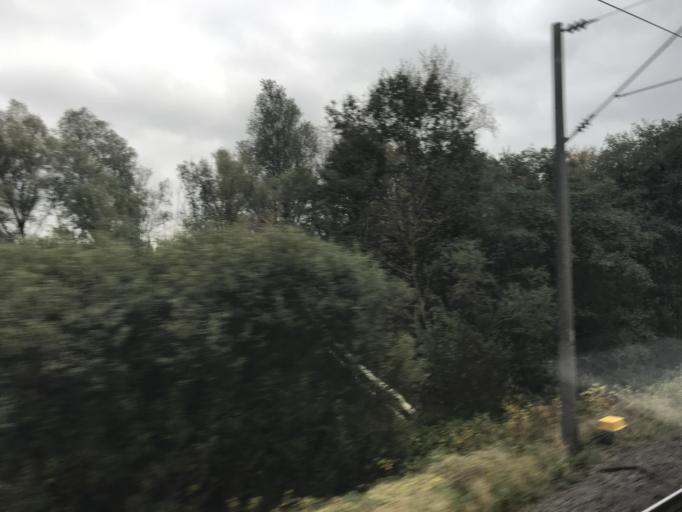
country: DE
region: Lower Saxony
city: Leer
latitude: 53.1915
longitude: 7.4642
